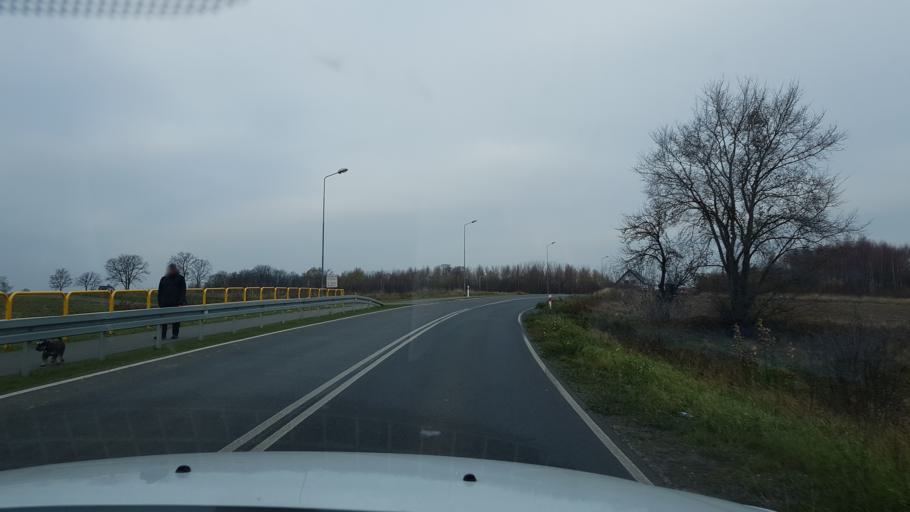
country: PL
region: West Pomeranian Voivodeship
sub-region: Powiat gryficki
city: Trzebiatow
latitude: 54.0694
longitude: 15.2587
